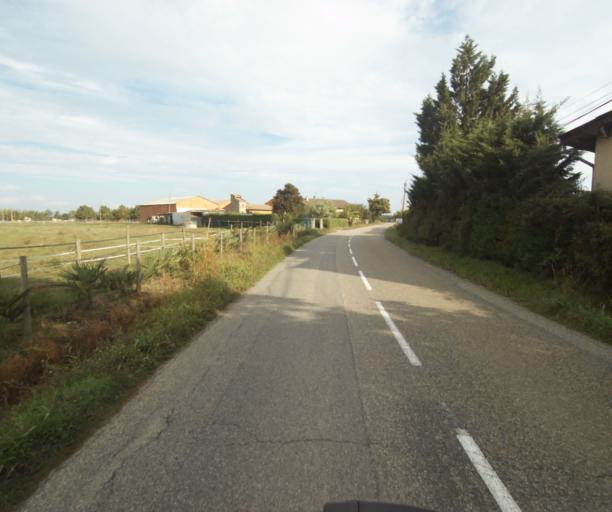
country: FR
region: Midi-Pyrenees
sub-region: Departement du Tarn-et-Garonne
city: Montech
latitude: 43.9702
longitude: 1.2318
